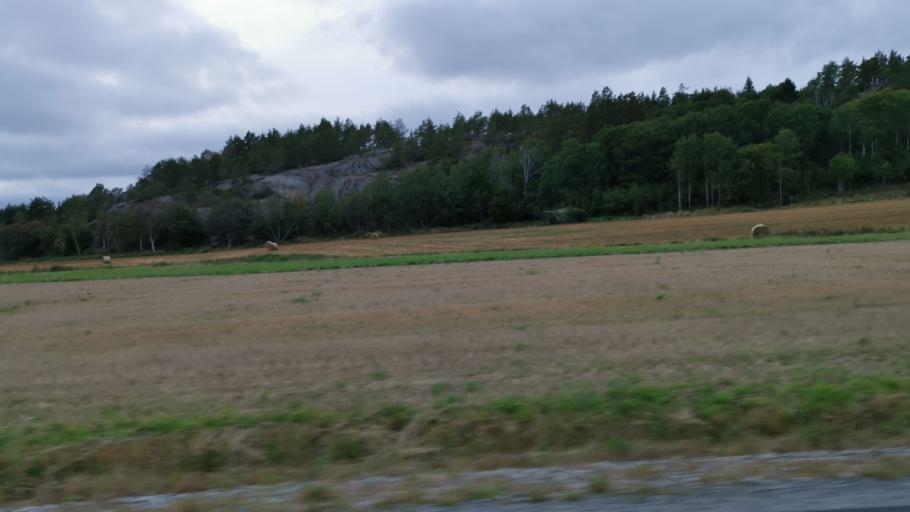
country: SE
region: Vaestra Goetaland
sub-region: Tanums Kommun
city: Tanumshede
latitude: 58.6527
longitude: 11.3423
